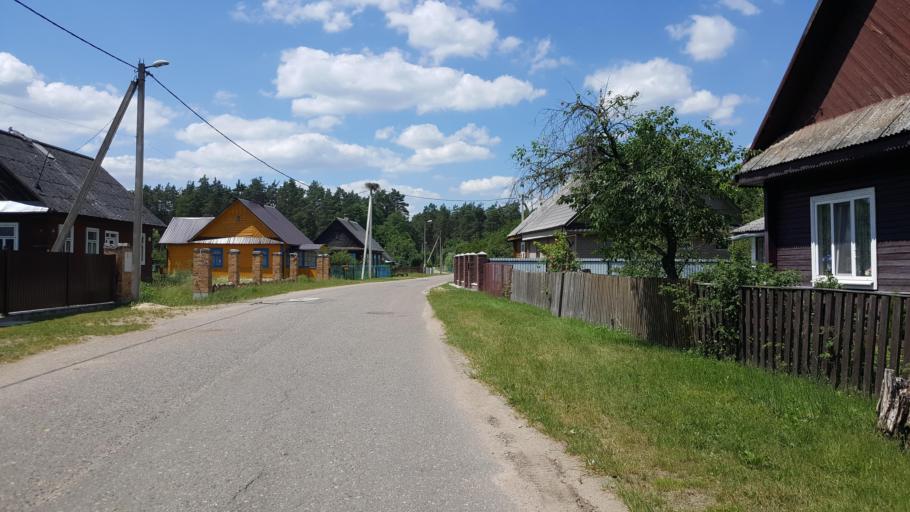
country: BY
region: Brest
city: Kamyanyuki
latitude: 52.5607
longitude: 23.7950
